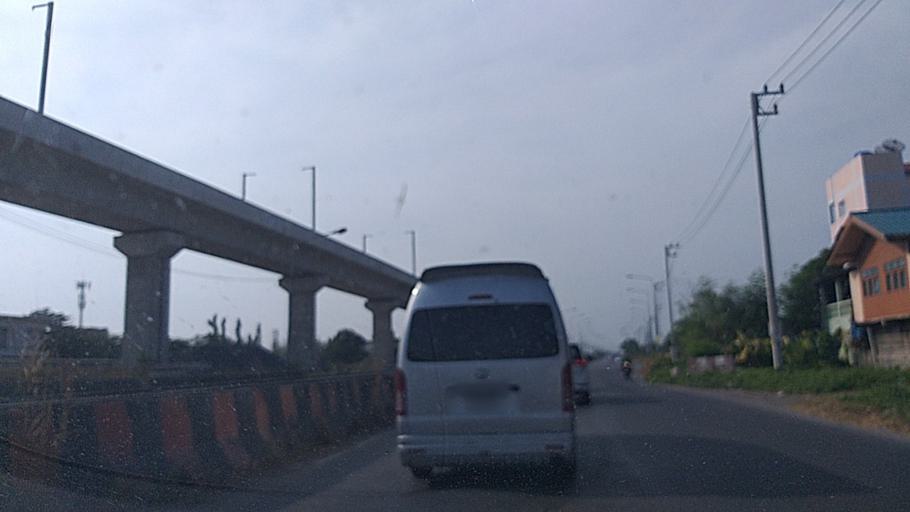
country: TH
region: Phra Nakhon Si Ayutthaya
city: Ban Bang Kadi Pathum Thani
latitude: 13.9848
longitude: 100.6026
